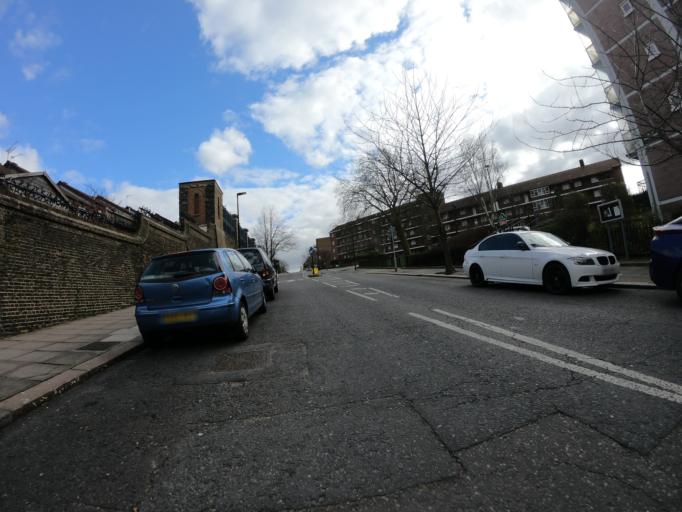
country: GB
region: England
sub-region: Greater London
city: Woolwich
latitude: 51.4897
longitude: 0.0534
